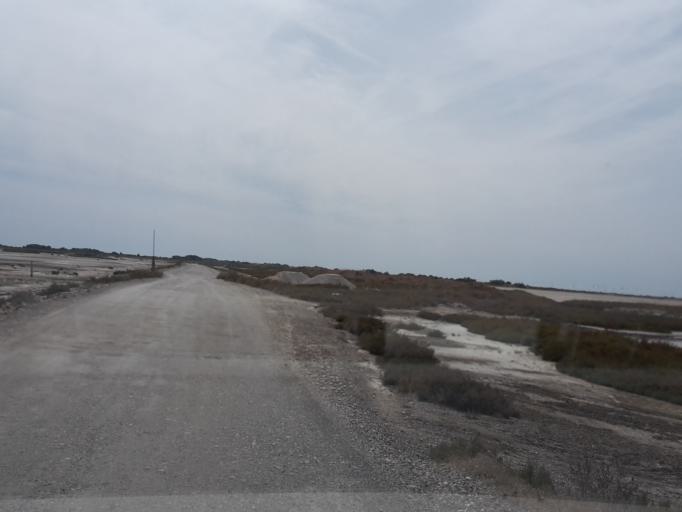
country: FR
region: Provence-Alpes-Cote d'Azur
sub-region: Departement des Bouches-du-Rhone
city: Saintes-Maries-de-la-Mer
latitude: 43.4182
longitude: 4.6217
